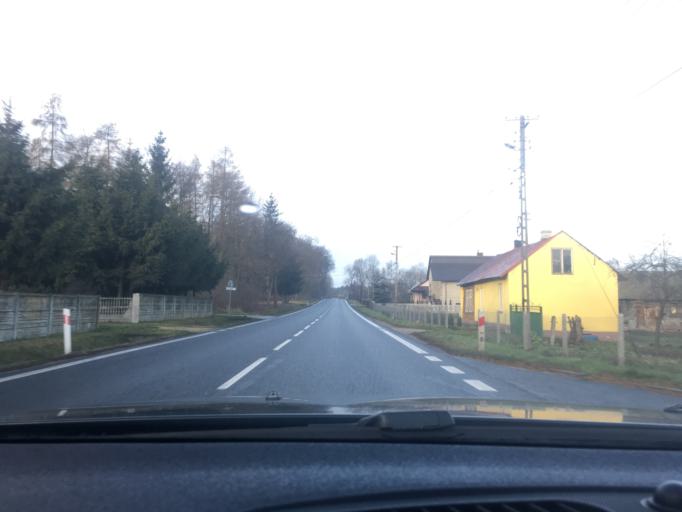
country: PL
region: Swietokrzyskie
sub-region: Powiat jedrzejowski
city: Imielno
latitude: 50.6223
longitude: 20.3981
